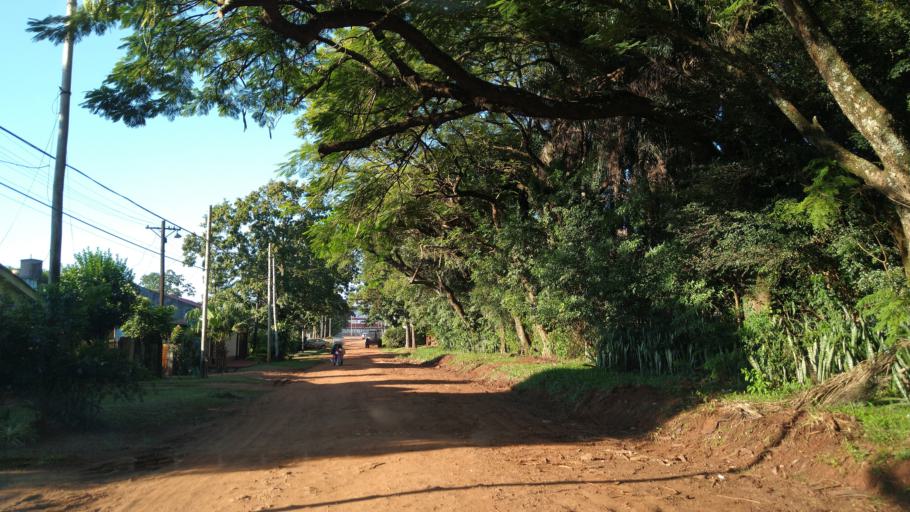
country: AR
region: Misiones
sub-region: Departamento de Capital
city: Posadas
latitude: -27.4040
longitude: -55.9236
